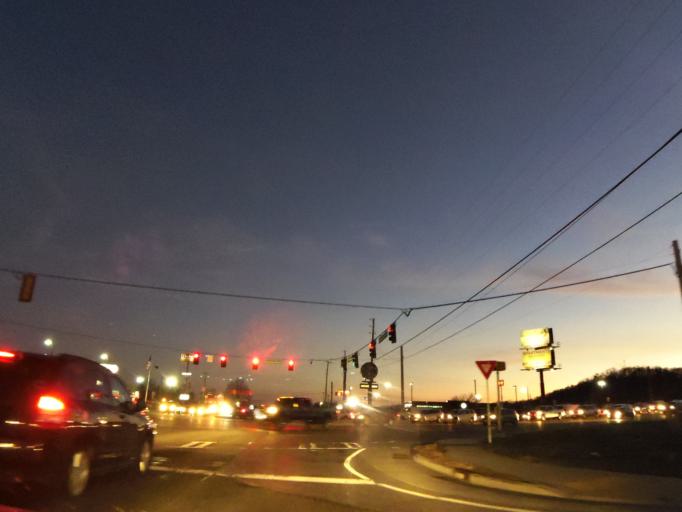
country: US
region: Georgia
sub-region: Whitfield County
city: Dalton
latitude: 34.7981
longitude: -84.9623
